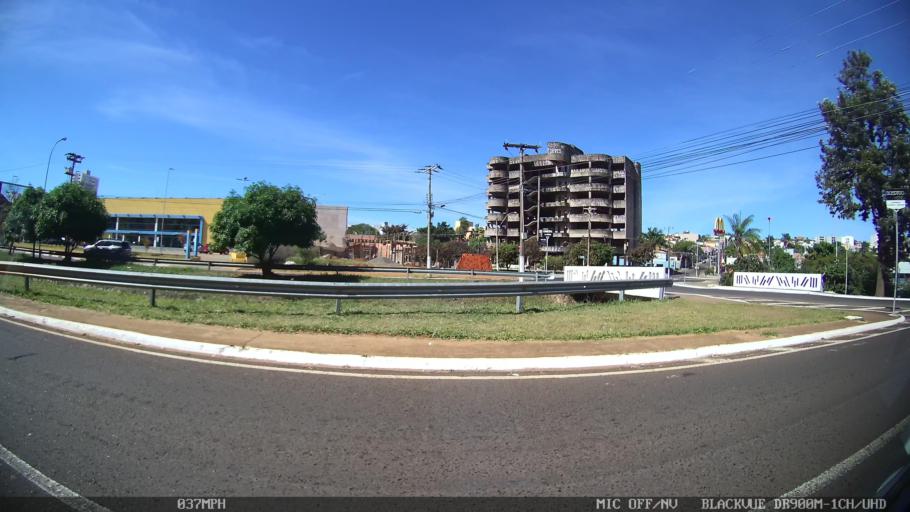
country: BR
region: Sao Paulo
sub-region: Franca
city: Franca
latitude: -20.5516
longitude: -47.4044
